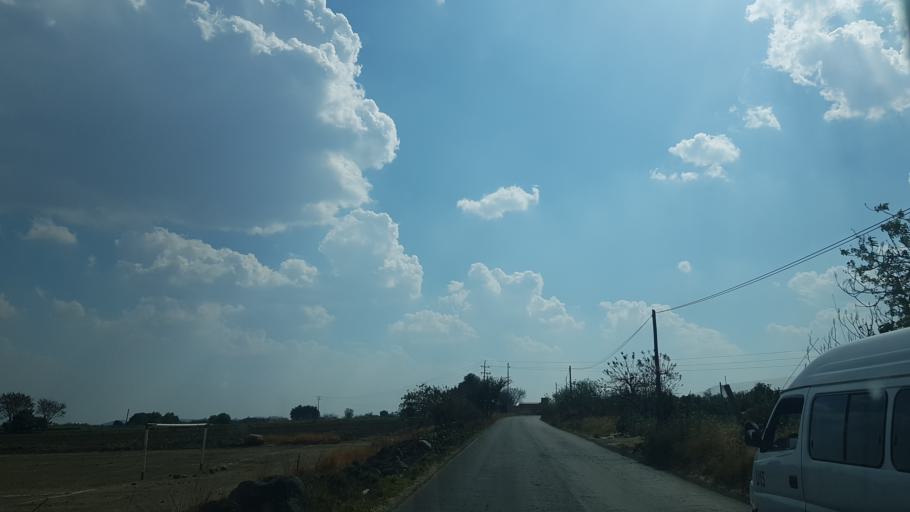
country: MX
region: Puebla
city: Atlixco
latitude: 18.9085
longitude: -98.4757
